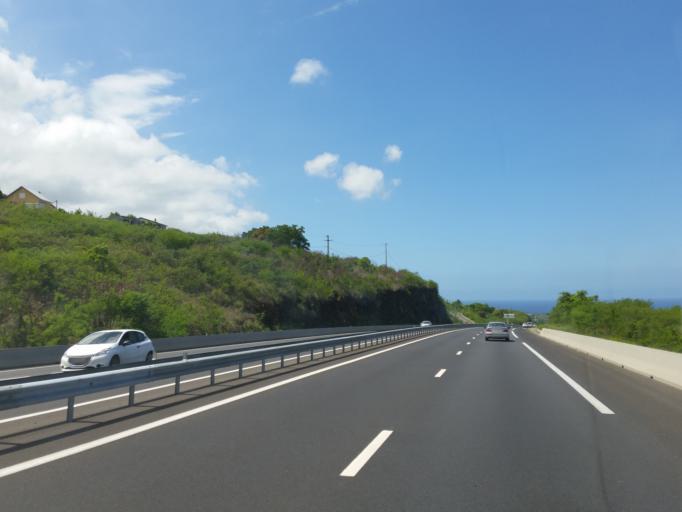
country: RE
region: Reunion
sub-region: Reunion
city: Saint-Leu
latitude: -21.1715
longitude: 55.2981
